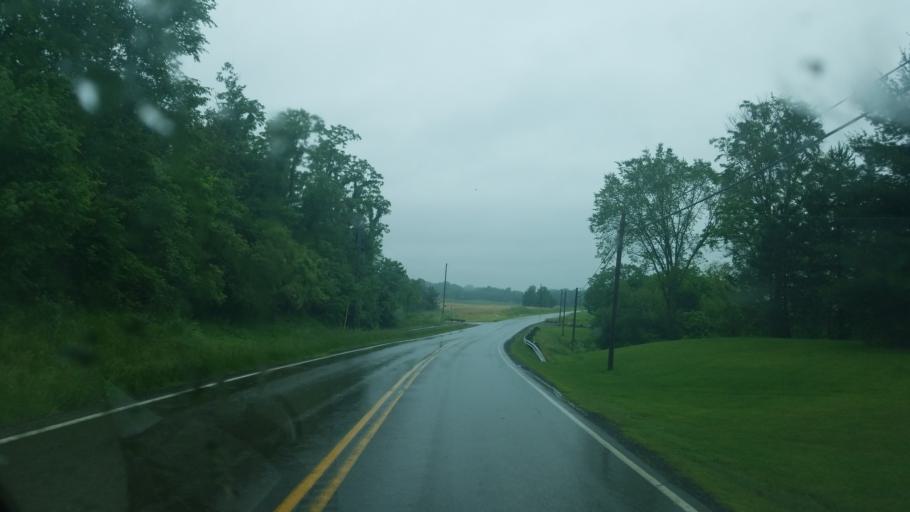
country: US
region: Ohio
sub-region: Huron County
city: Greenwich
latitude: 40.9395
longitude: -82.5507
